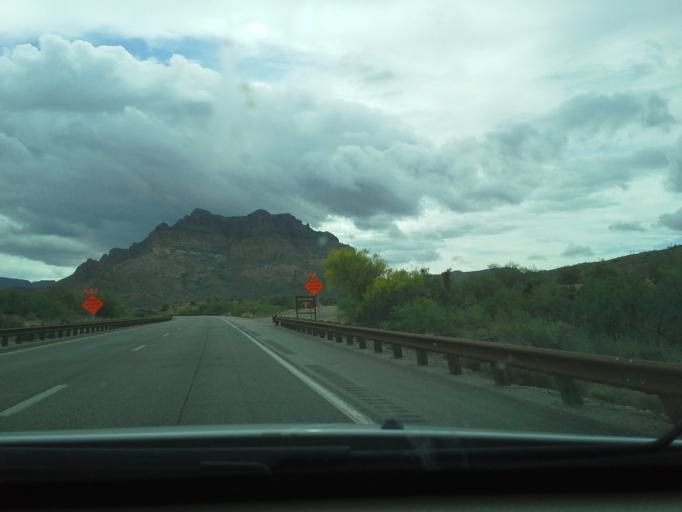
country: US
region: Arizona
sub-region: Pinal County
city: Superior
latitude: 33.2732
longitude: -111.1958
